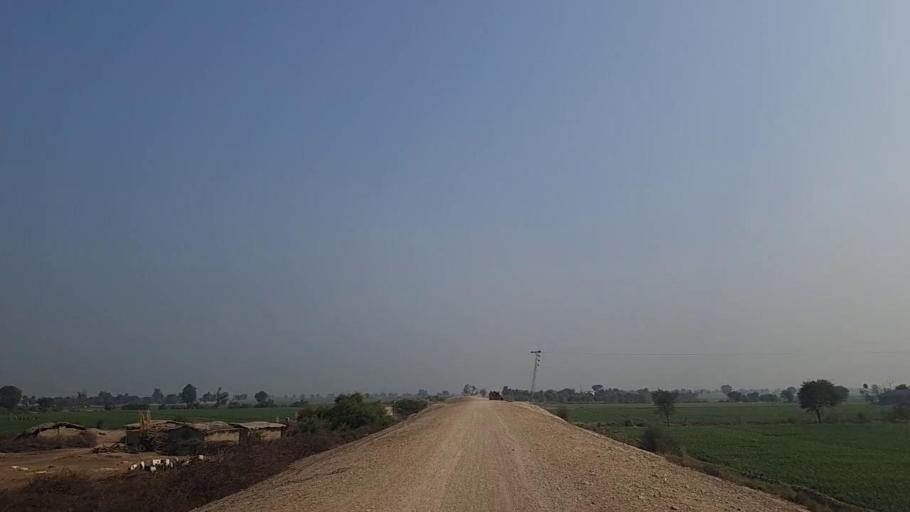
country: PK
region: Sindh
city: Sann
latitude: 26.0905
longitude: 68.1520
